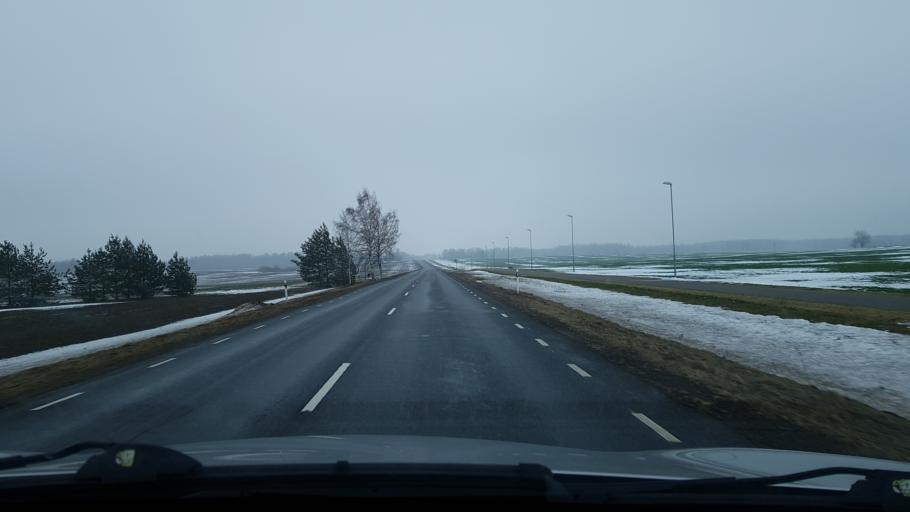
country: EE
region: Valgamaa
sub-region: Torva linn
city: Torva
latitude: 58.2199
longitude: 25.9011
